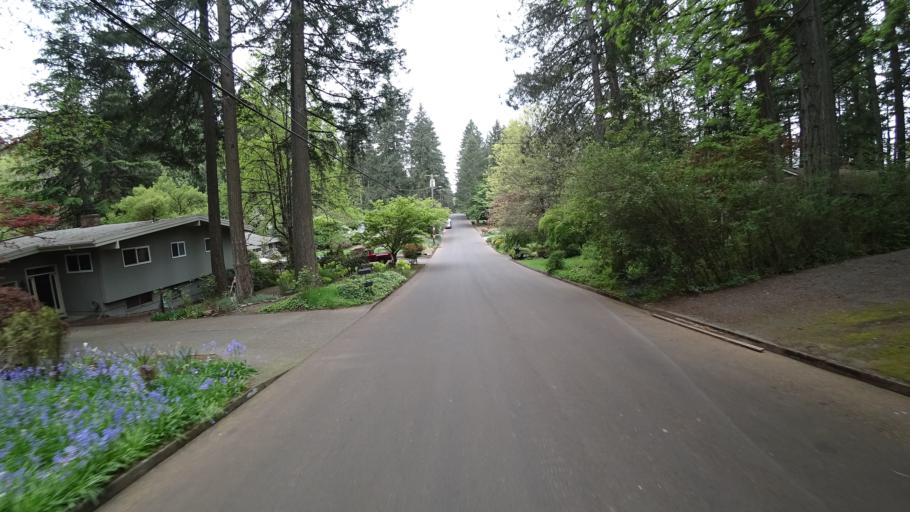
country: US
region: Oregon
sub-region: Washington County
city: Beaverton
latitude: 45.4628
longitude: -122.8176
